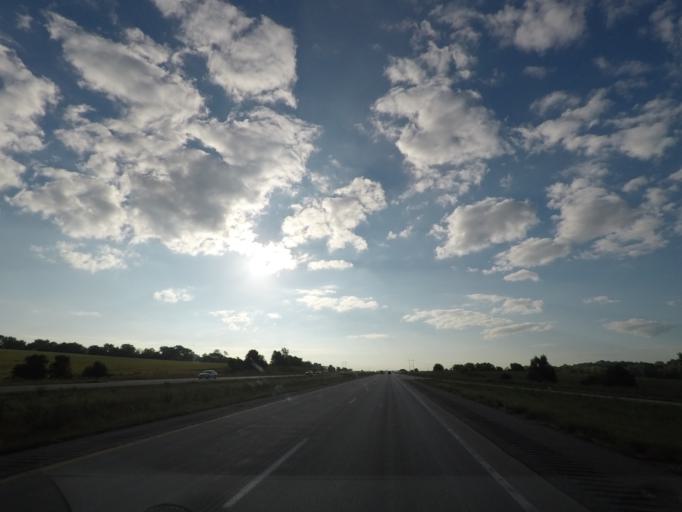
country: US
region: Iowa
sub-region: Warren County
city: Norwalk
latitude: 41.5052
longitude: -93.6402
